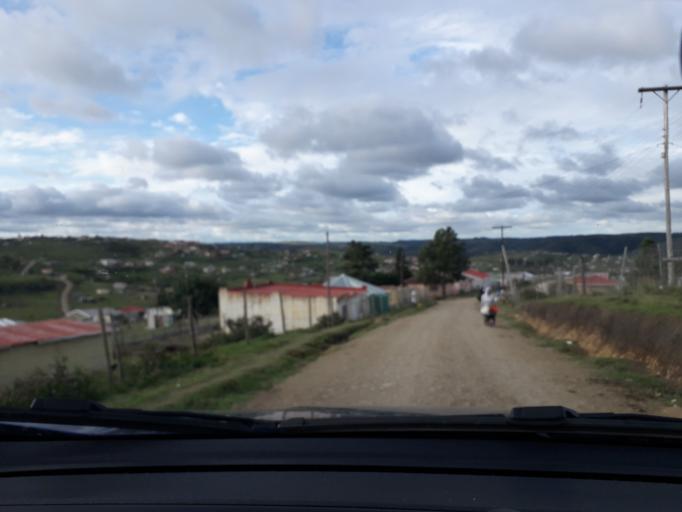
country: ZA
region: Eastern Cape
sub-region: Buffalo City Metropolitan Municipality
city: East London
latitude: -32.8050
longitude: 27.9603
